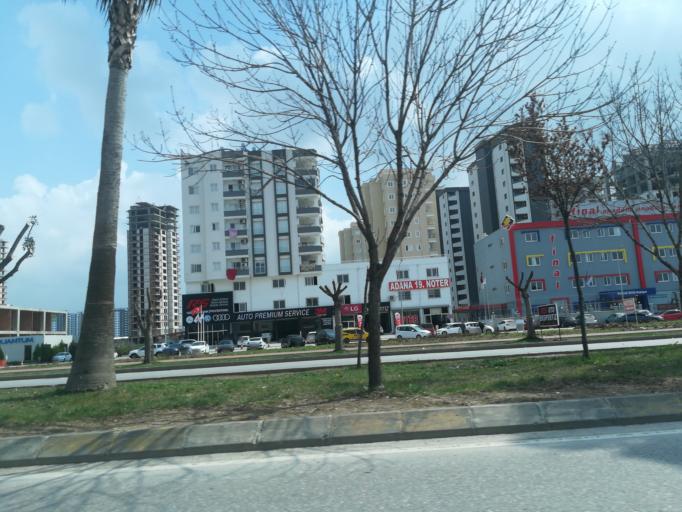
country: TR
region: Adana
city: Seyhan
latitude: 37.0108
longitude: 35.2501
